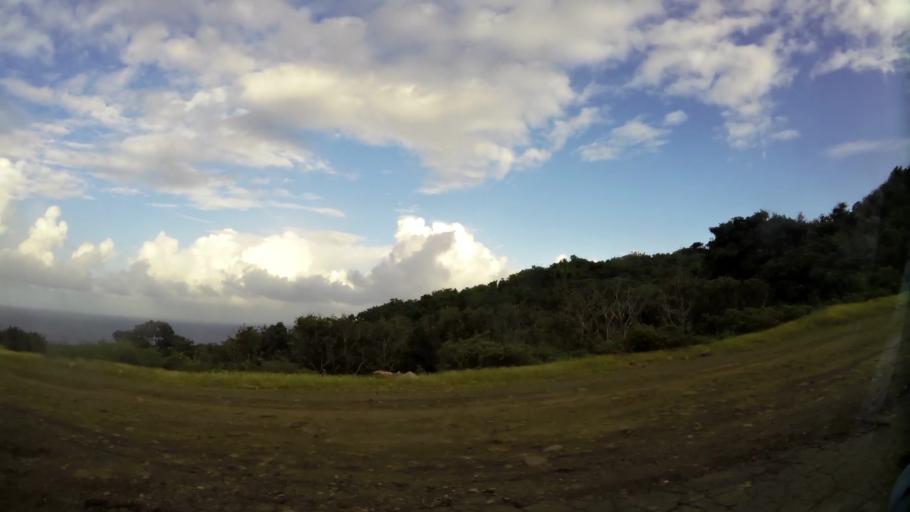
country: MS
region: Saint Peter
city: Brades
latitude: 16.7710
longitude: -62.1710
